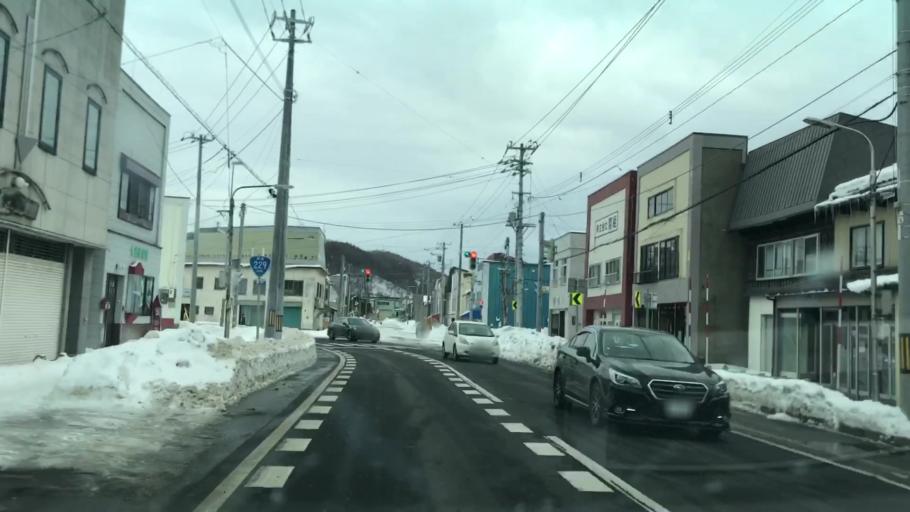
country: JP
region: Hokkaido
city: Yoichi
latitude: 43.2041
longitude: 140.7714
